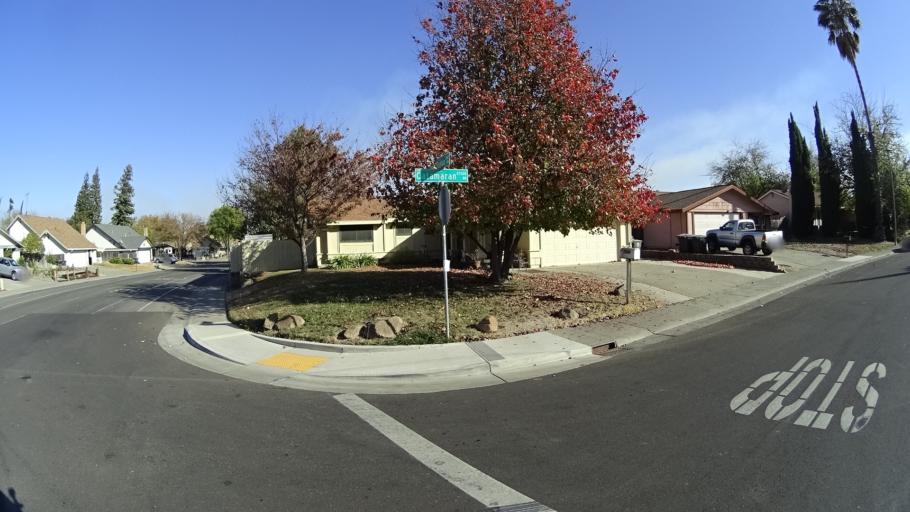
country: US
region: California
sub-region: Sacramento County
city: Antelope
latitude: 38.6987
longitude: -121.3253
